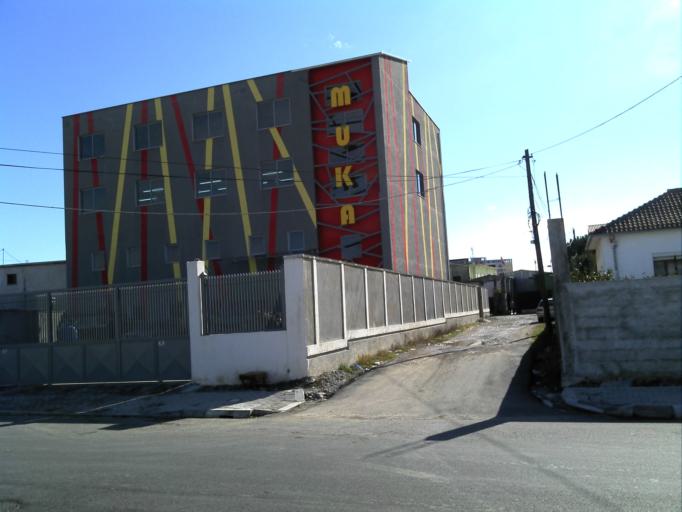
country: AL
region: Shkoder
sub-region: Rrethi i Shkodres
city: Shkoder
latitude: 42.0788
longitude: 19.5175
